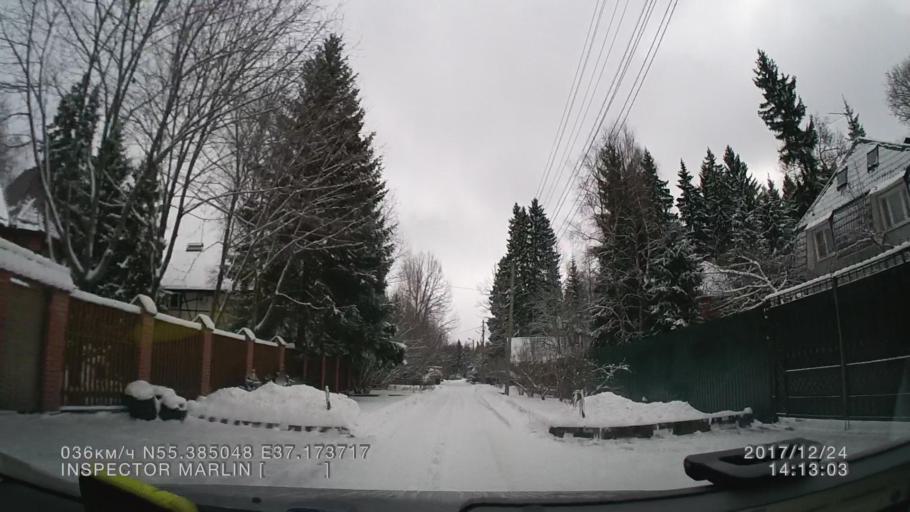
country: RU
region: Moskovskaya
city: Troitsk
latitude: 55.3850
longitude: 37.1740
